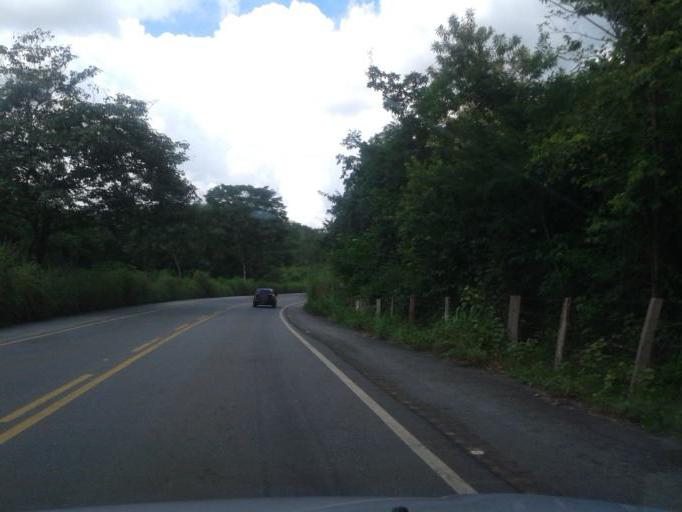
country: BR
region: Goias
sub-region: Goias
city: Goias
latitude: -15.8803
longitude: -50.1027
